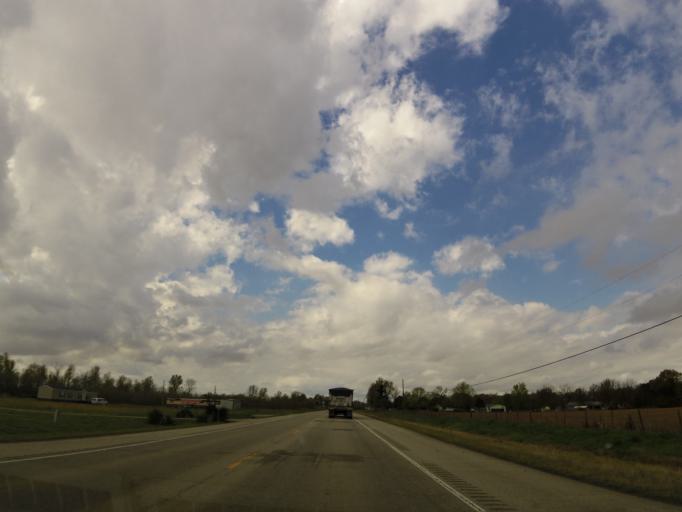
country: US
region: Arkansas
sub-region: Clay County
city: Corning
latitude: 36.4639
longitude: -90.5728
